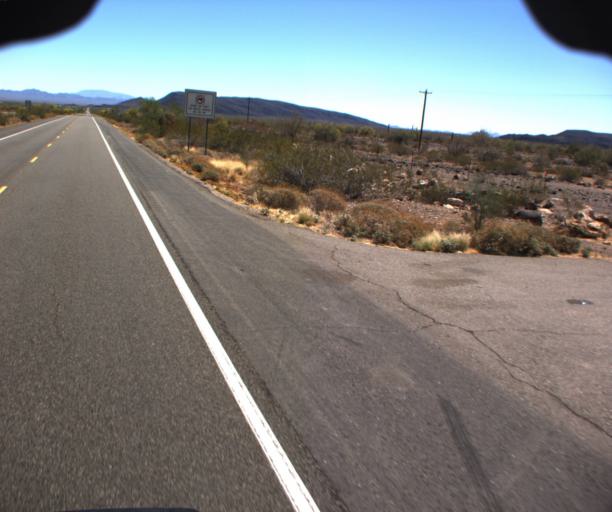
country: US
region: Arizona
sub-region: La Paz County
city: Quartzsite
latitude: 33.6659
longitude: -114.0009
